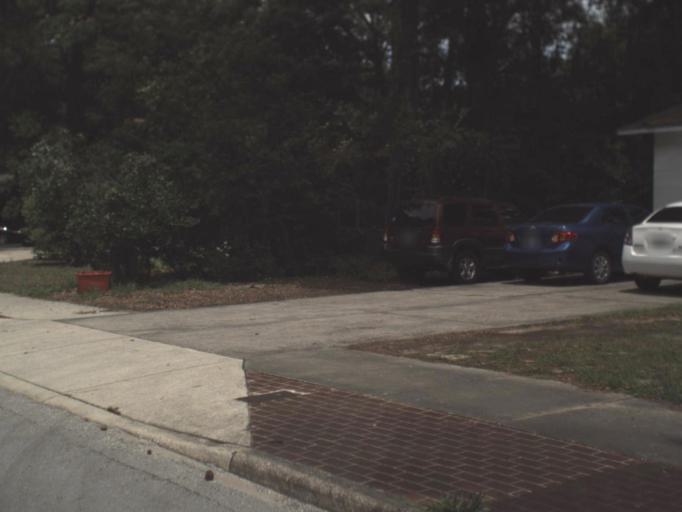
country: US
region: Florida
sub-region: Alachua County
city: Gainesville
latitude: 29.6523
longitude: -82.3688
